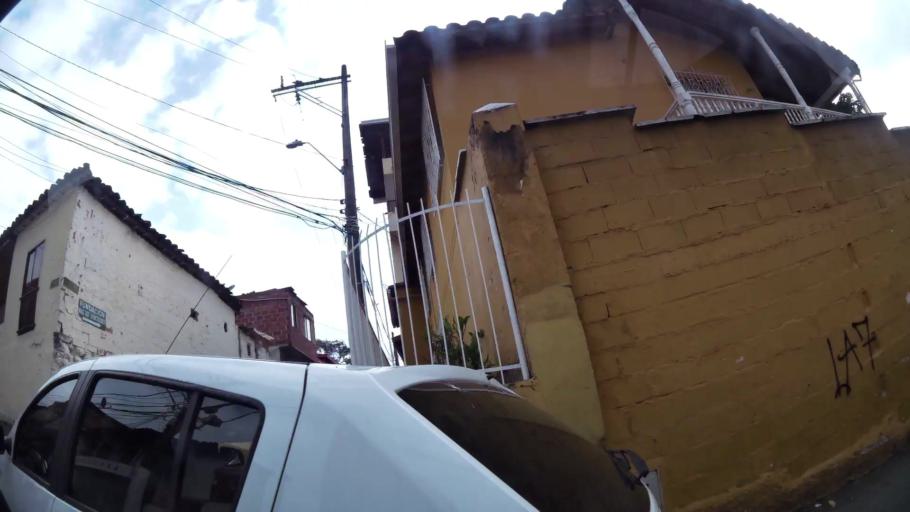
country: CO
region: Antioquia
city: Medellin
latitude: 6.2799
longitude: -75.6001
